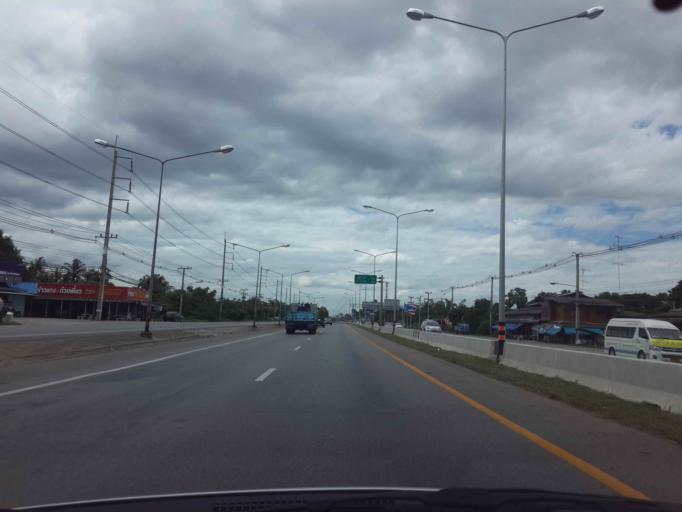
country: TH
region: Phetchaburi
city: Phetchaburi
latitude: 13.1459
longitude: 99.8556
